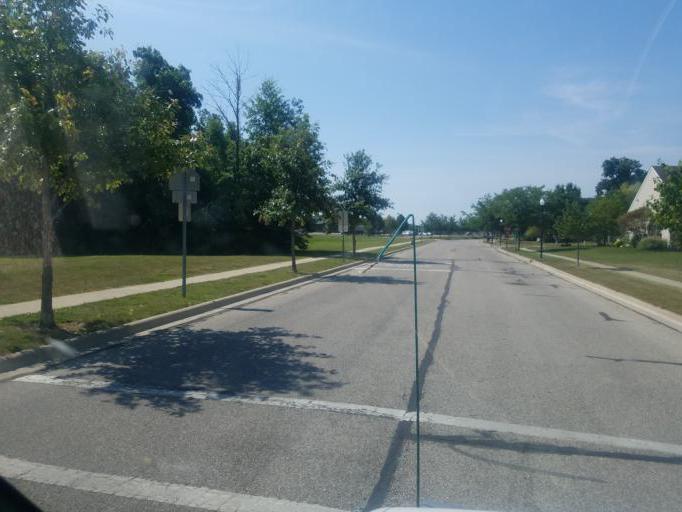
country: US
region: Ohio
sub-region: Union County
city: Marysville
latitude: 40.2670
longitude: -83.3853
